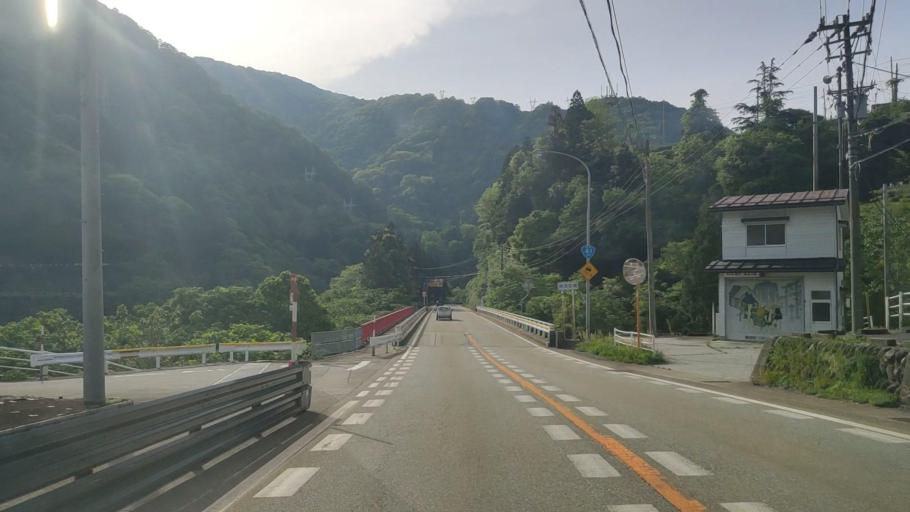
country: JP
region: Toyama
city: Yatsuomachi-higashikumisaka
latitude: 36.4355
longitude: 137.2761
